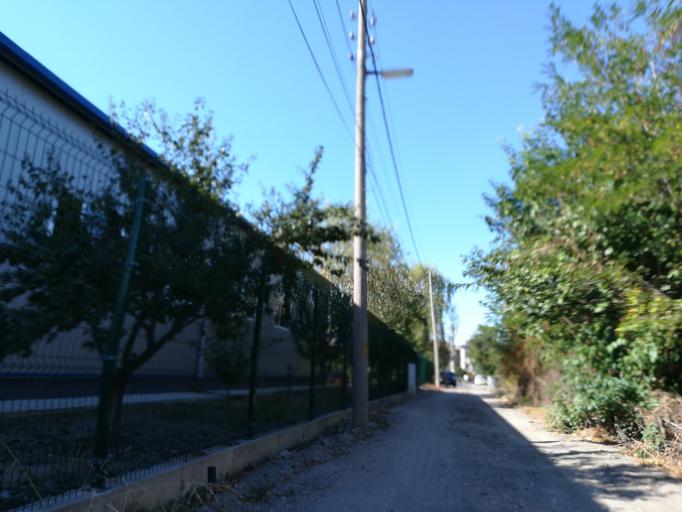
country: BG
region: Stara Zagora
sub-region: Obshtina Chirpan
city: Chirpan
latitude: 42.0938
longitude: 25.2313
